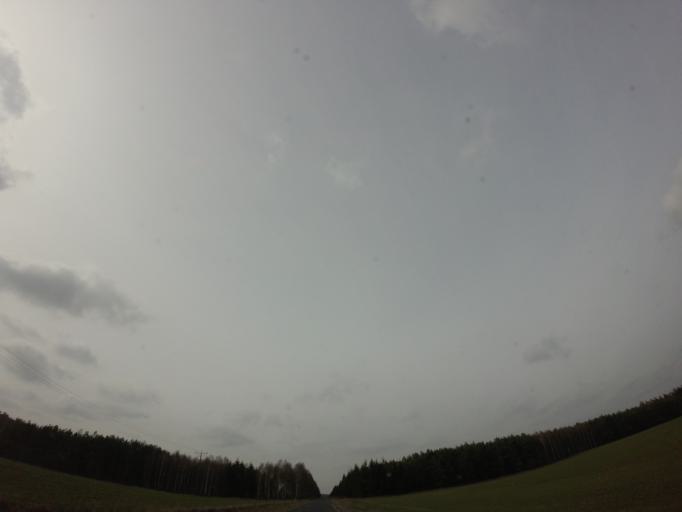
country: PL
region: West Pomeranian Voivodeship
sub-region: Powiat drawski
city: Wierzchowo
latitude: 53.4357
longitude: 16.1843
